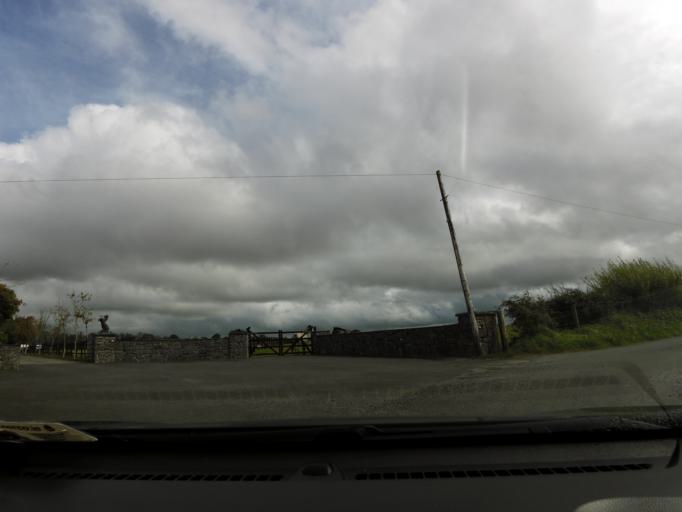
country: IE
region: Connaught
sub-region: County Galway
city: Loughrea
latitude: 53.3039
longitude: -8.5943
